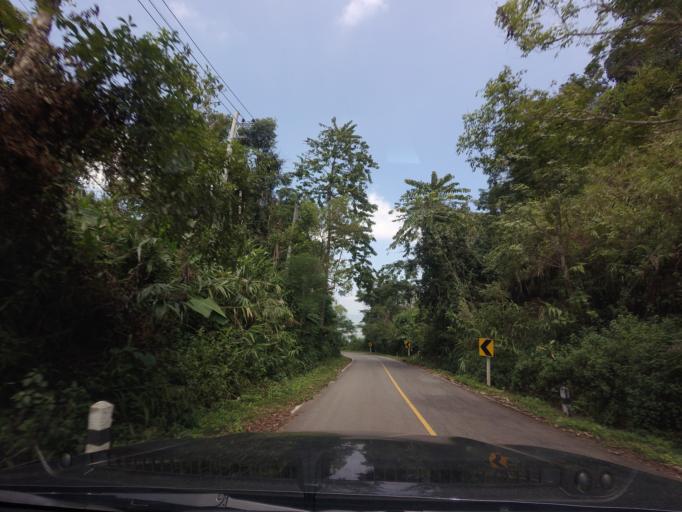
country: TH
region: Loei
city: Na Haeo
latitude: 17.4851
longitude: 100.9064
